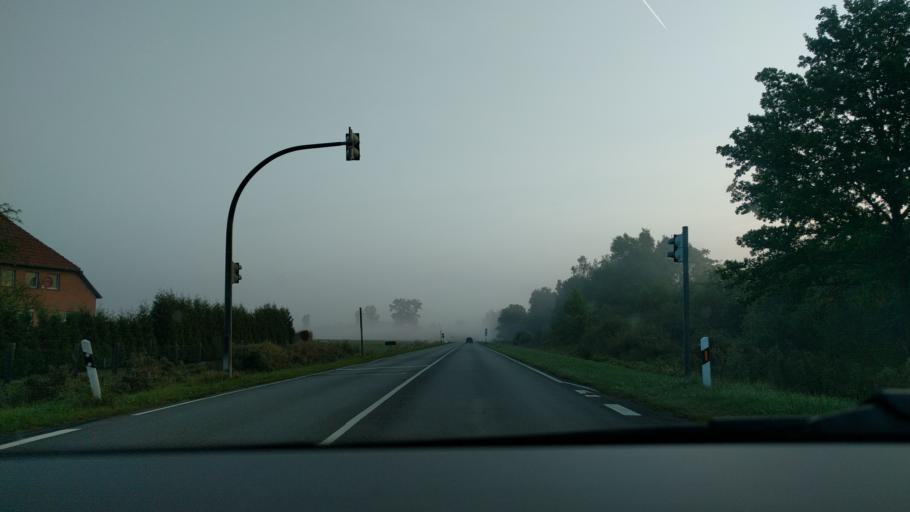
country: DE
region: Lower Saxony
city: Osloss
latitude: 52.4336
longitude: 10.6644
